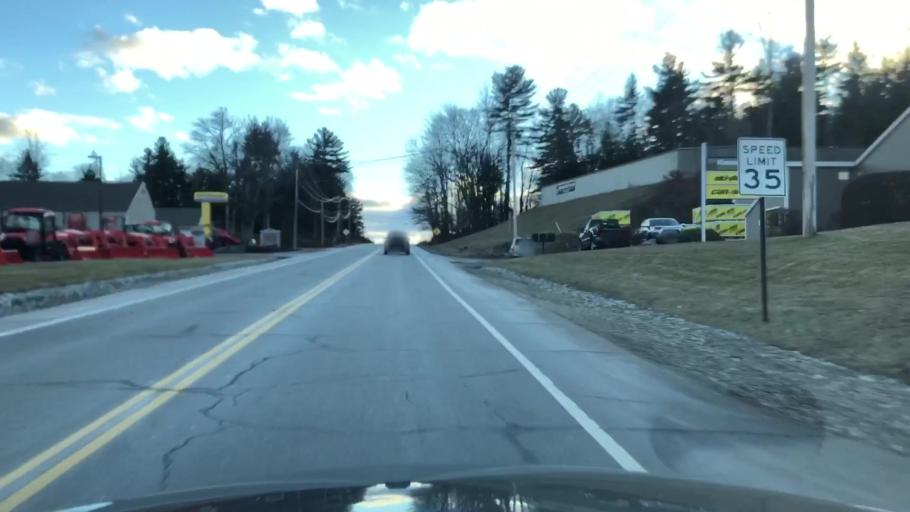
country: US
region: New Hampshire
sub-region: Hillsborough County
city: Milford
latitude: 42.8137
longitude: -71.6471
